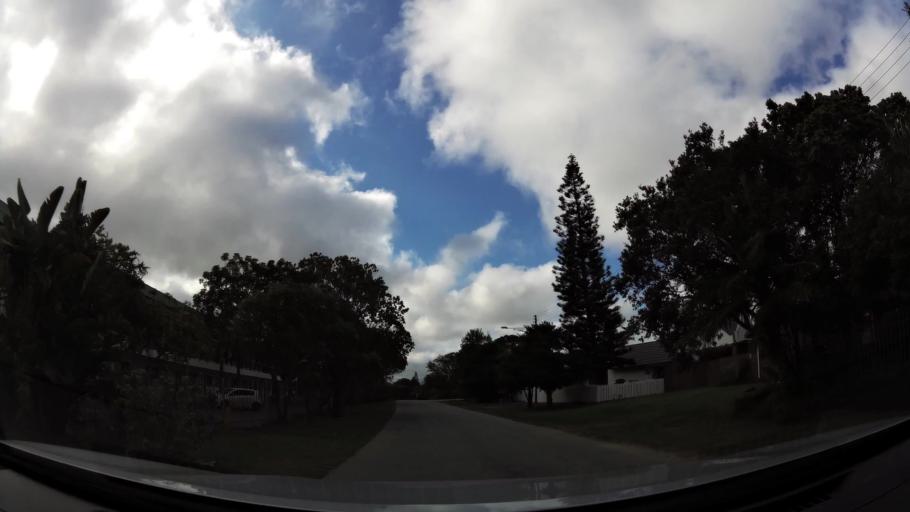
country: ZA
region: Western Cape
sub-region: Eden District Municipality
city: Plettenberg Bay
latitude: -34.0736
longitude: 23.3681
